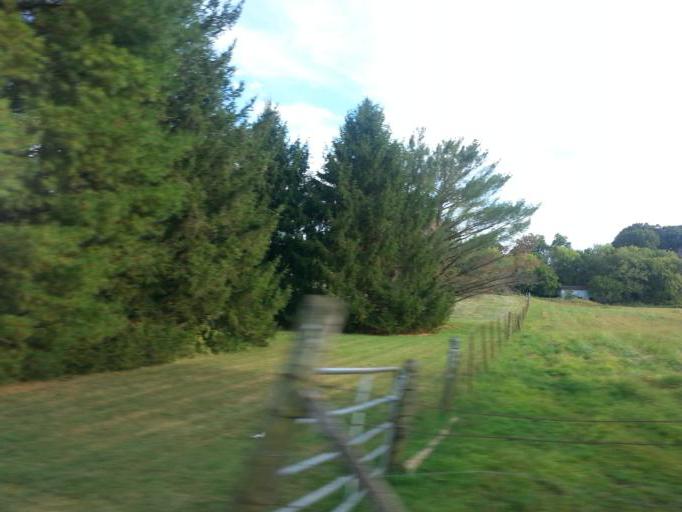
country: US
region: Tennessee
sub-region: Blount County
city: Wildwood
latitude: 35.8204
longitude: -83.8904
